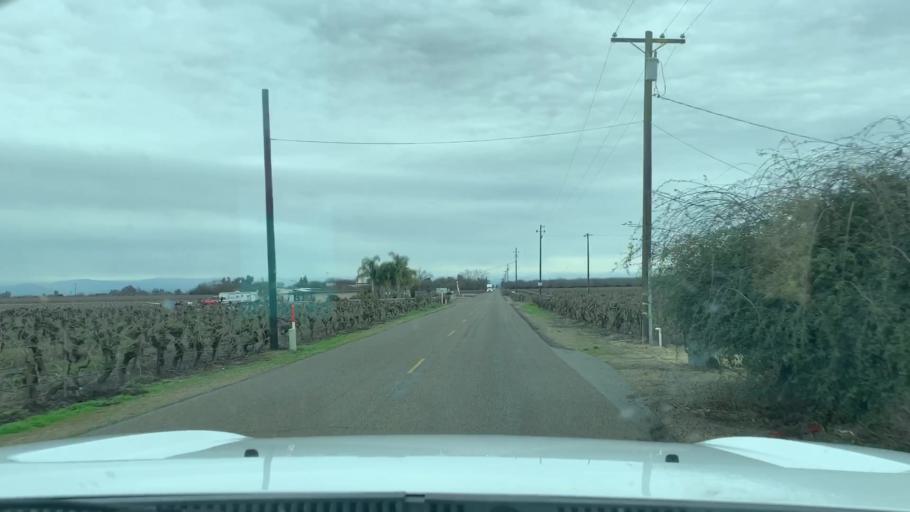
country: US
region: California
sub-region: Fresno County
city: Fowler
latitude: 36.5472
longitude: -119.6974
